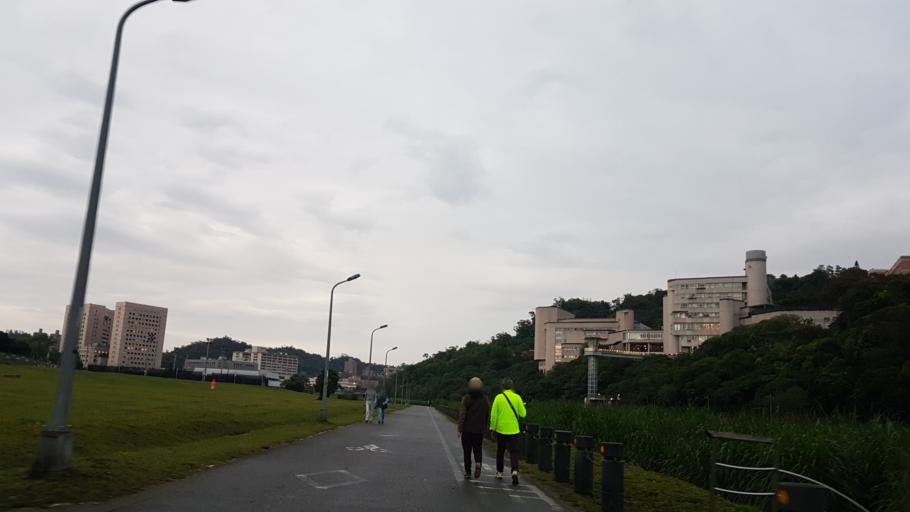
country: TW
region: Taipei
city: Taipei
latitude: 24.9814
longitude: 121.5690
